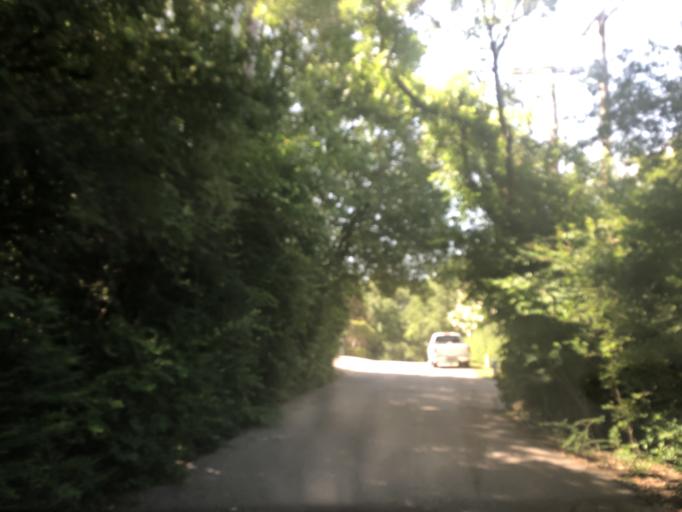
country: US
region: Texas
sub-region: Dallas County
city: University Park
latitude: 32.8747
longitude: -96.8195
